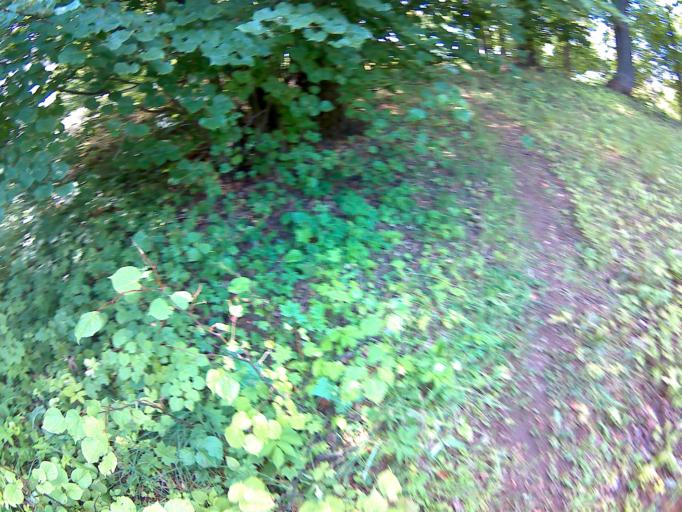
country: RU
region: Nizjnij Novgorod
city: Nizhniy Novgorod
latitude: 56.2301
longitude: 43.9254
